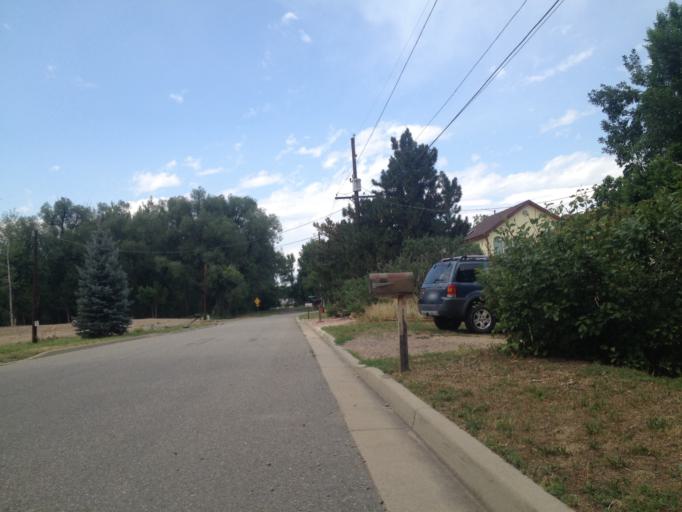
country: US
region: Colorado
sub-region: Boulder County
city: Superior
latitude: 39.9506
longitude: -105.1693
